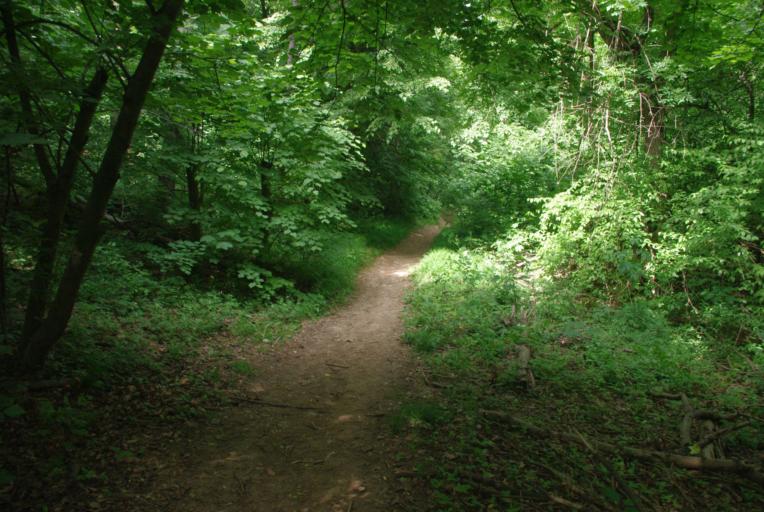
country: HU
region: Pest
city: Pilisszentivan
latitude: 47.5920
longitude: 18.8724
